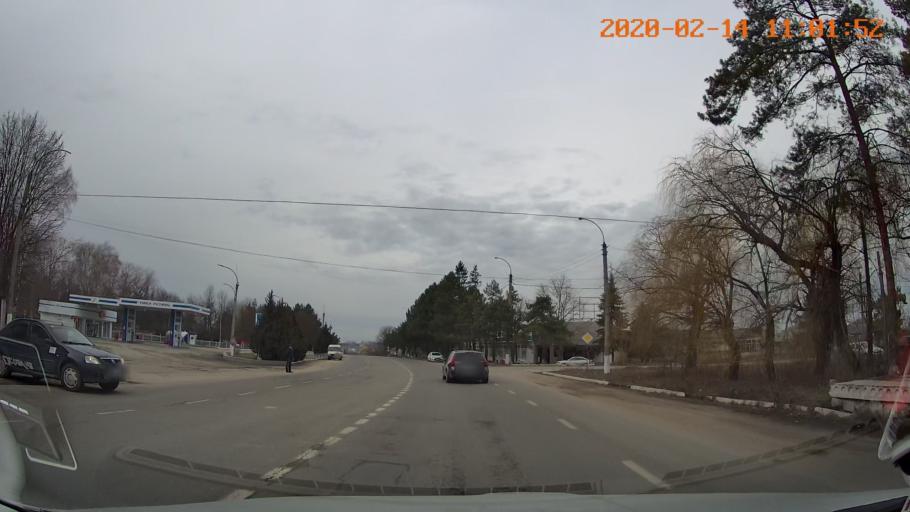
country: MD
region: Raionul Edinet
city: Edinet
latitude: 48.1622
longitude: 27.3253
